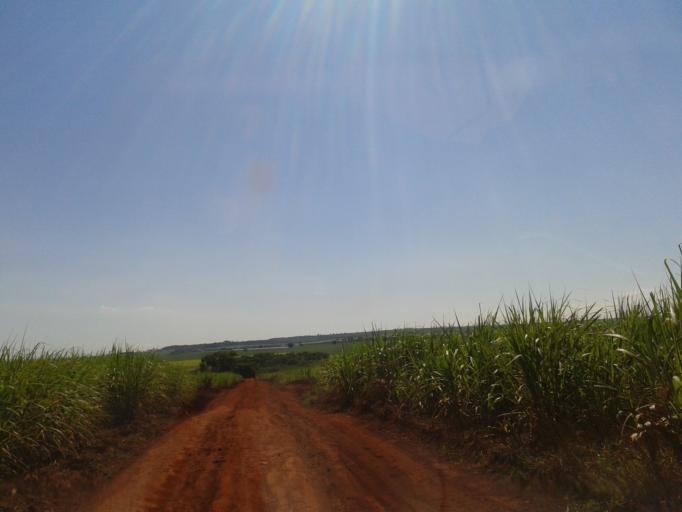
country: BR
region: Minas Gerais
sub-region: Centralina
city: Centralina
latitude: -18.6216
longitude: -49.2587
